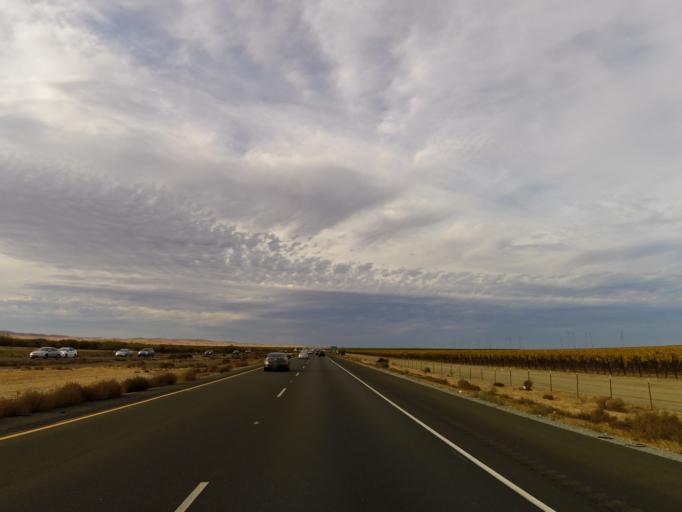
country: US
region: California
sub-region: Kings County
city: Kettleman City
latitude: 35.9181
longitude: -119.8949
